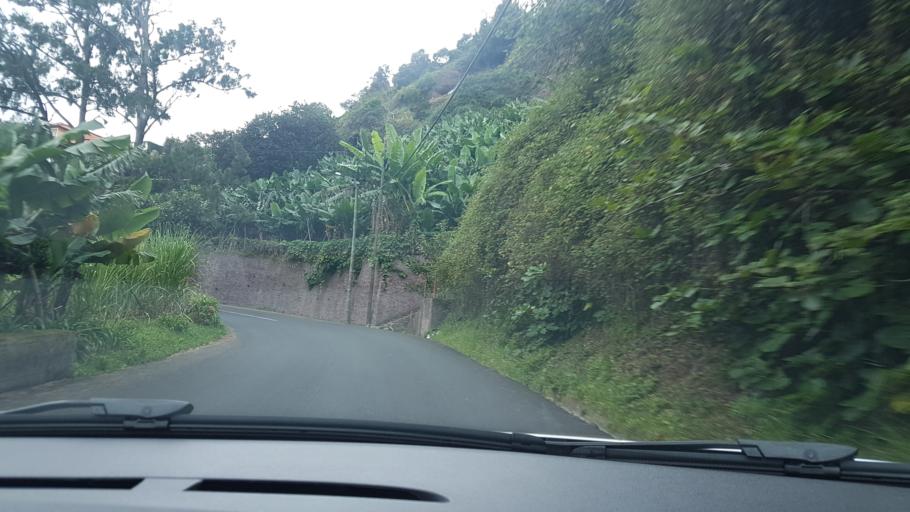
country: PT
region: Madeira
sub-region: Santana
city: Santana
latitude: 32.7736
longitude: -16.8390
